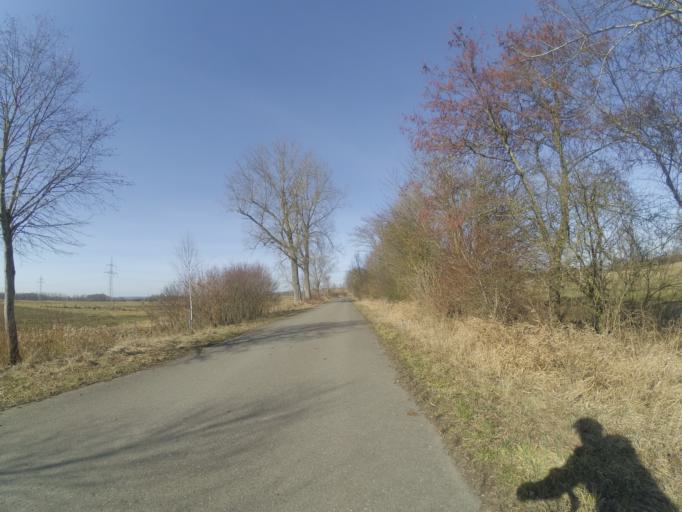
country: DE
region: Baden-Wuerttemberg
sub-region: Tuebingen Region
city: Rammingen
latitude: 48.4980
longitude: 10.1944
